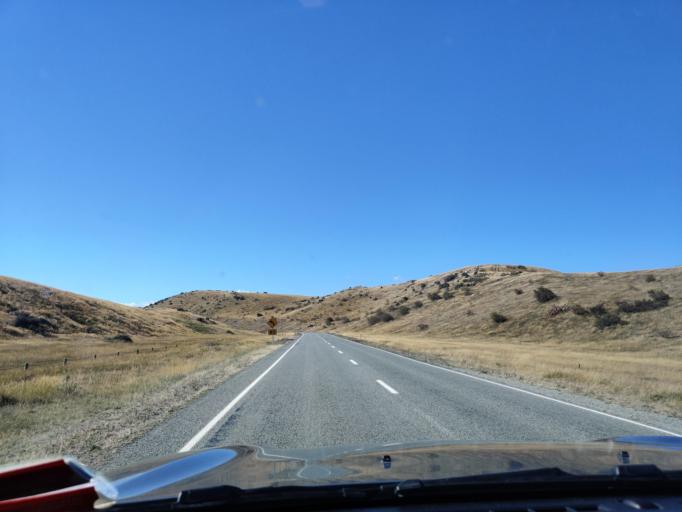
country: NZ
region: Canterbury
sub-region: Timaru District
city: Pleasant Point
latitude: -44.1839
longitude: 170.1550
